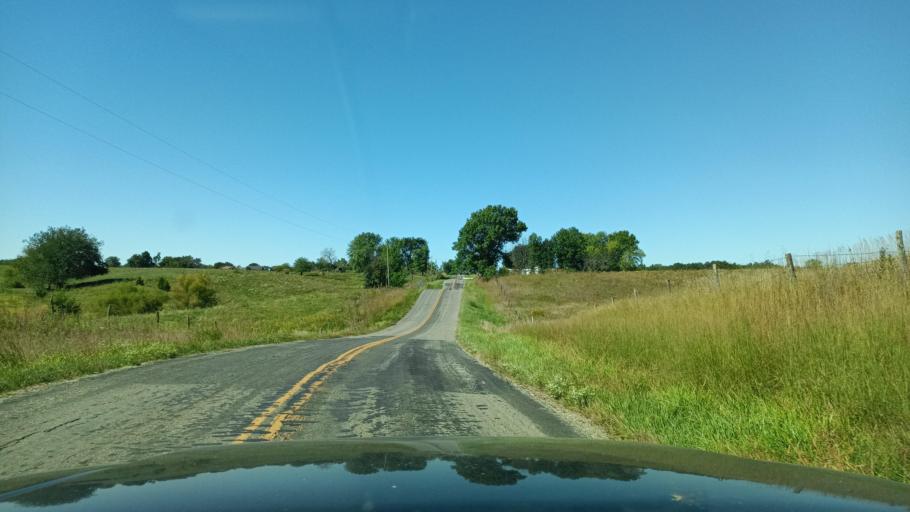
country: US
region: Missouri
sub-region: Scotland County
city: Memphis
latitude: 40.3538
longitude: -92.2943
